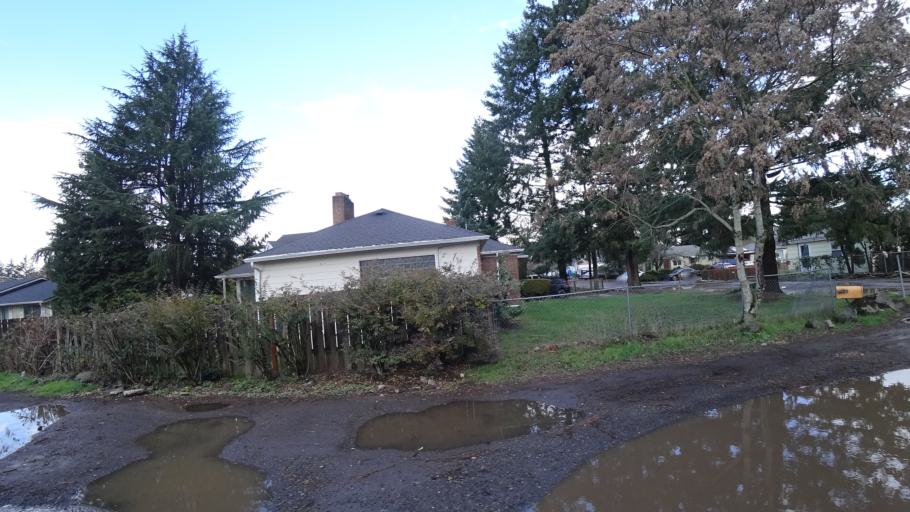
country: US
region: Oregon
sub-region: Multnomah County
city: Lents
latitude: 45.5299
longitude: -122.5405
